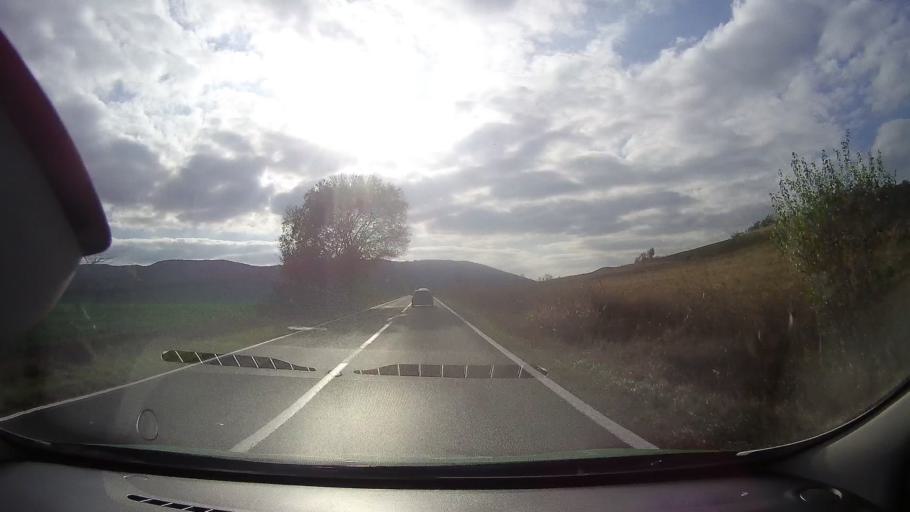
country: RO
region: Tulcea
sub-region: Comuna Nalbant
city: Nicolae Balcescu
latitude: 44.9711
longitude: 28.5397
